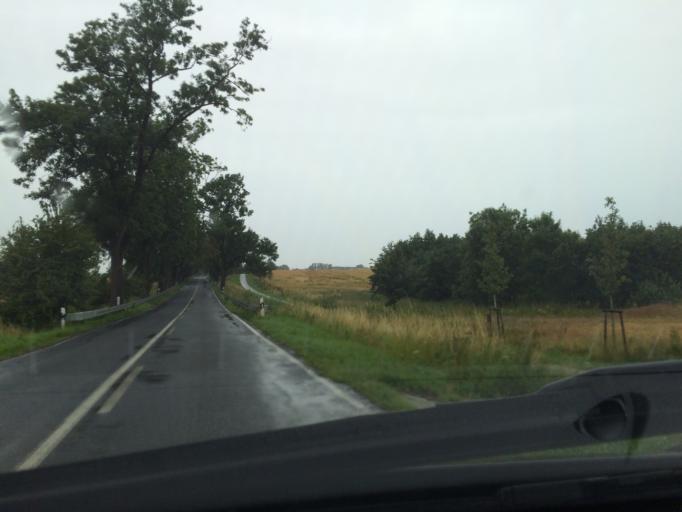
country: DE
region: Mecklenburg-Vorpommern
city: Kramerhof
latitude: 54.3574
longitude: 13.0376
